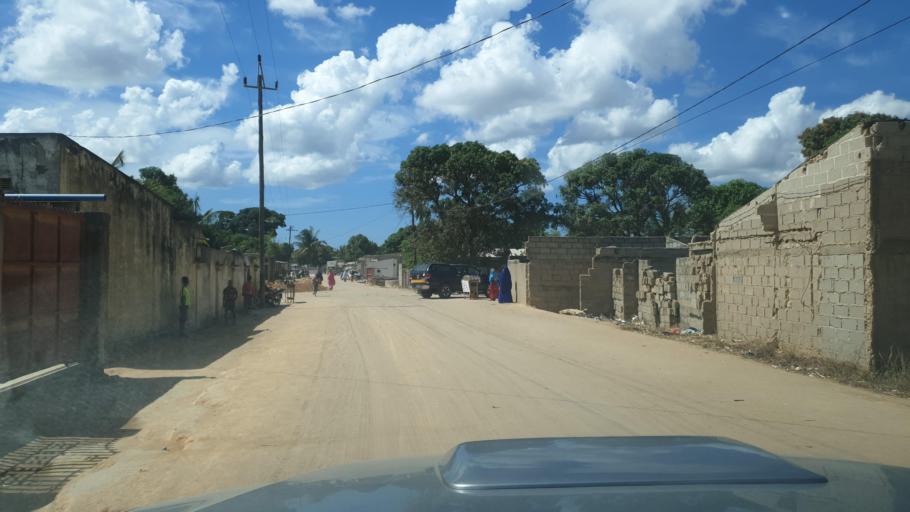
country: MZ
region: Nampula
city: Nacala
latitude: -14.5658
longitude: 40.7000
